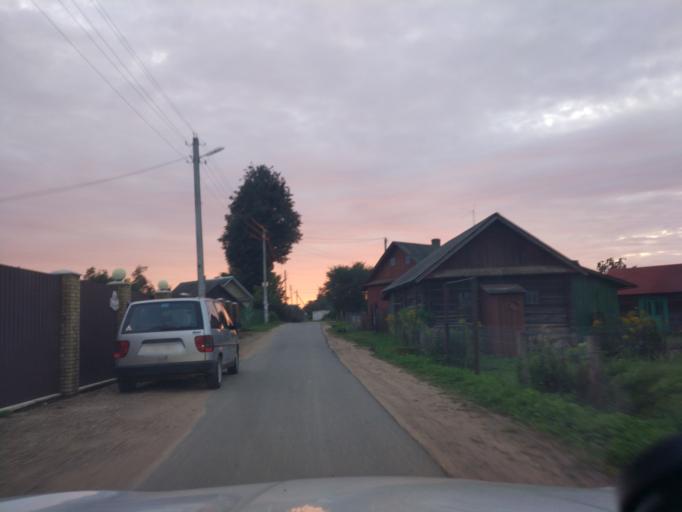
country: BY
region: Minsk
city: Astrashytski Haradok
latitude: 54.0843
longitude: 27.7033
